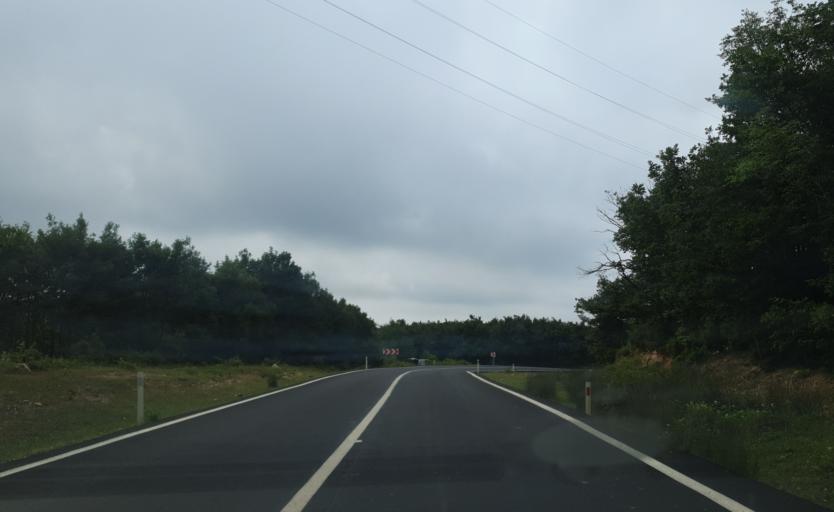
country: TR
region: Kirklareli
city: Salmydessus
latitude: 41.5979
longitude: 28.0832
